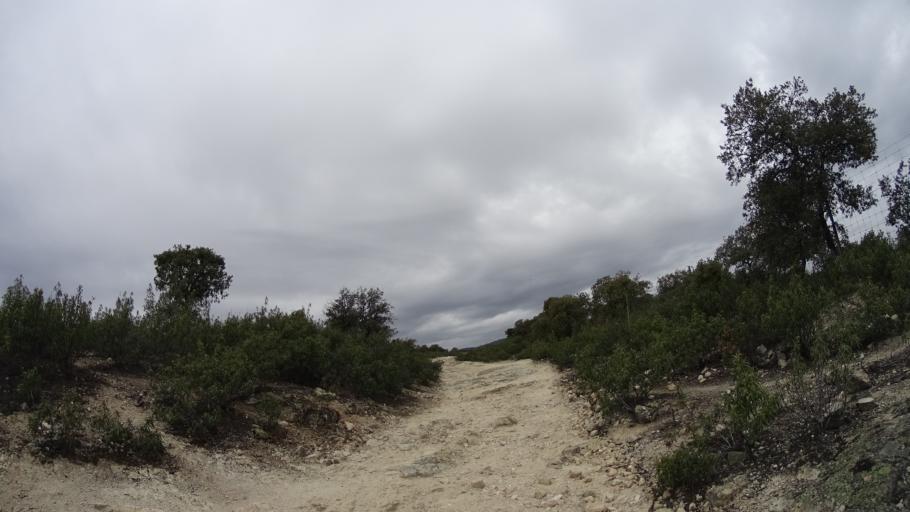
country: ES
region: Madrid
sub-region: Provincia de Madrid
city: Hoyo de Manzanares
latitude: 40.5944
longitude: -3.8851
